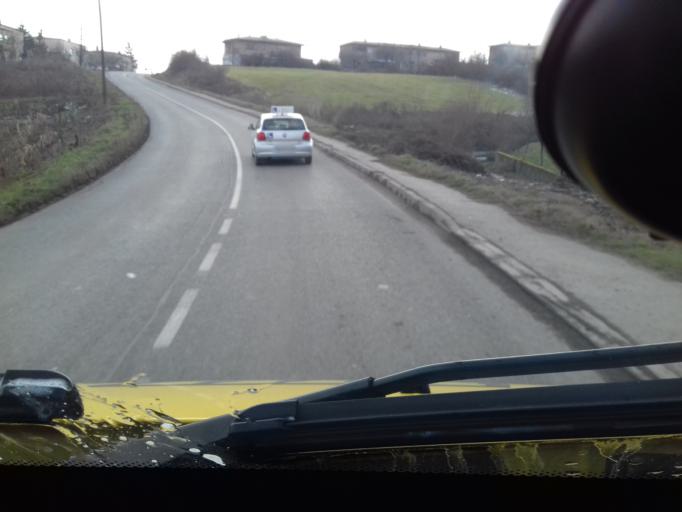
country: BA
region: Federation of Bosnia and Herzegovina
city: Zenica
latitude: 44.2226
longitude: 17.8923
